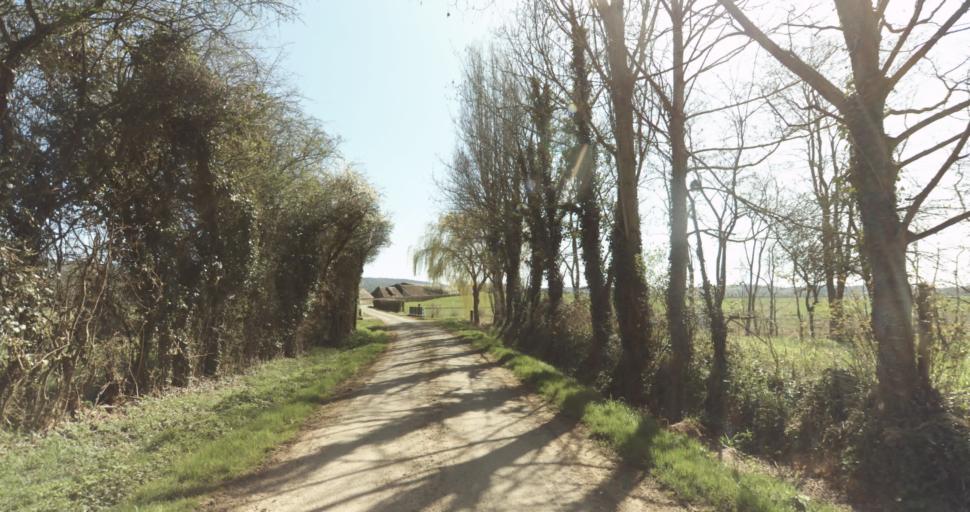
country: FR
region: Lower Normandy
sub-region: Departement du Calvados
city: Saint-Pierre-sur-Dives
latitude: 49.0081
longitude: 0.0168
